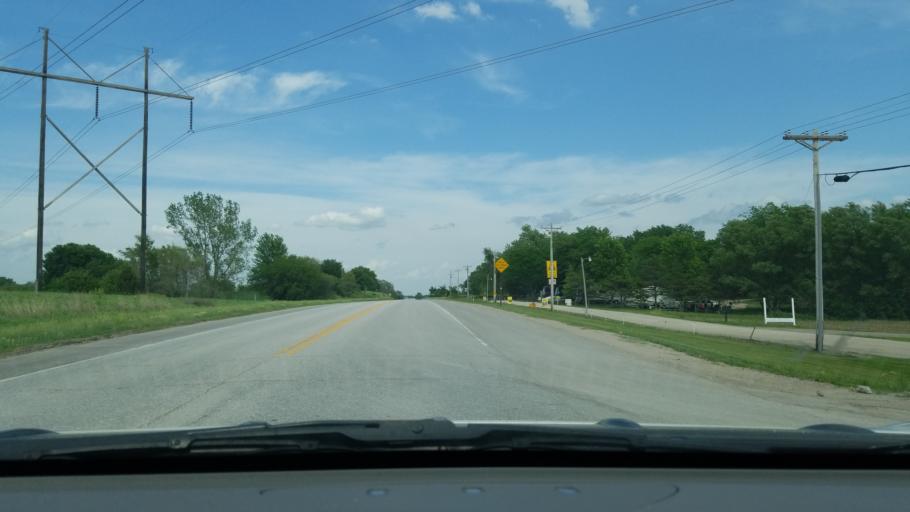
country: US
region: Nebraska
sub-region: Sarpy County
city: Gretna
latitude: 41.0947
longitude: -96.2665
